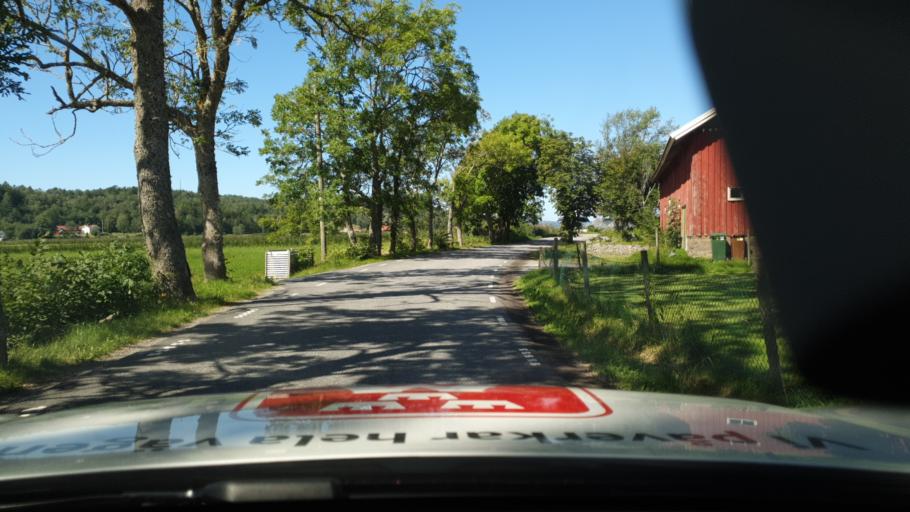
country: SE
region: Vaestra Goetaland
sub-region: Kungalvs Kommun
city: Kode
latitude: 57.9161
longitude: 11.7980
